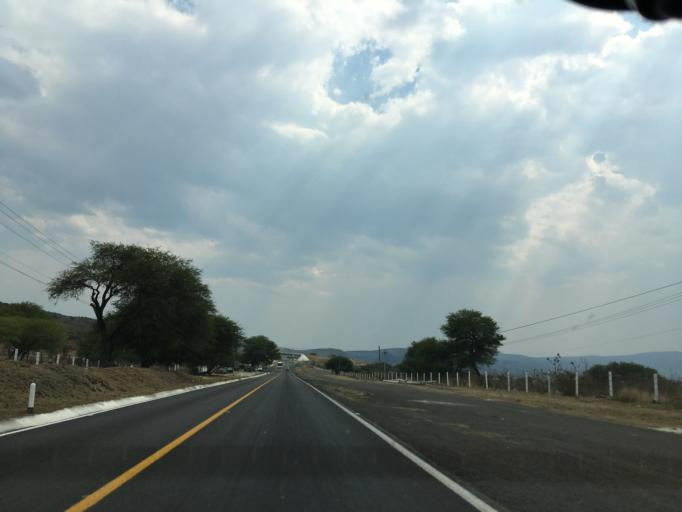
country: MX
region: Michoacan
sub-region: Cuitzeo
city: San Juan Benito Juarez (San Juan Tararameo)
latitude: 19.9183
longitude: -101.1443
